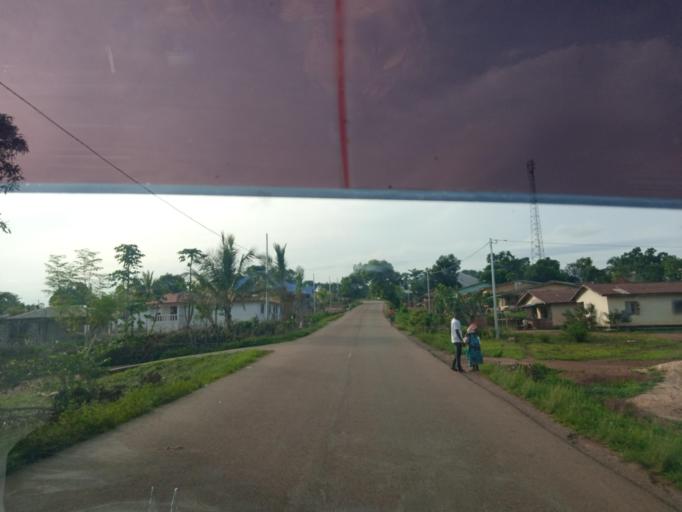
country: SL
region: Southern Province
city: Largo
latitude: 8.1984
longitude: -12.0589
